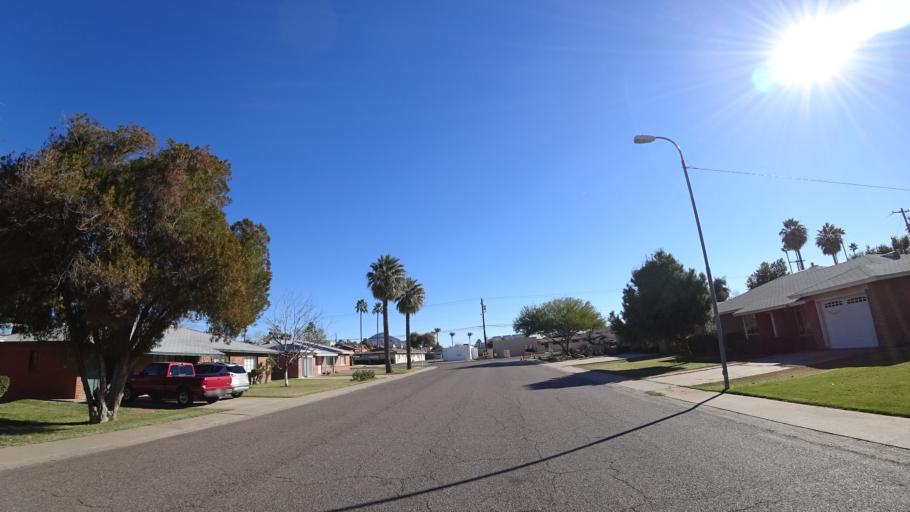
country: US
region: Arizona
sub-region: Maricopa County
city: Phoenix
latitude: 33.4967
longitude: -112.0266
